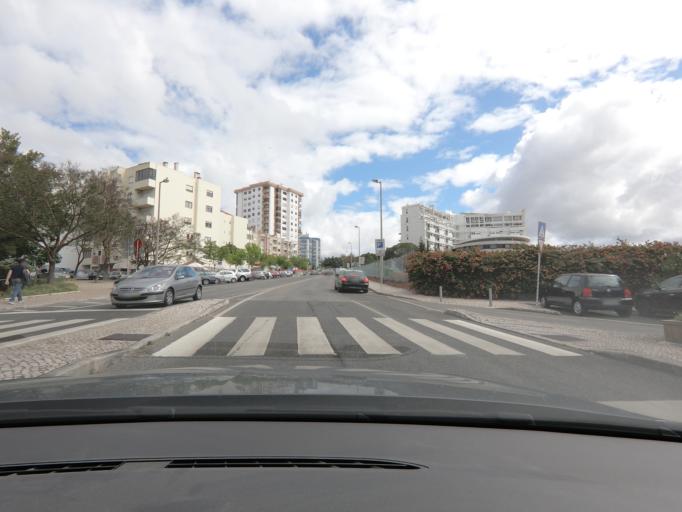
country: PT
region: Lisbon
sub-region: Oeiras
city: Carnaxide
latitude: 38.7257
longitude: -9.2345
